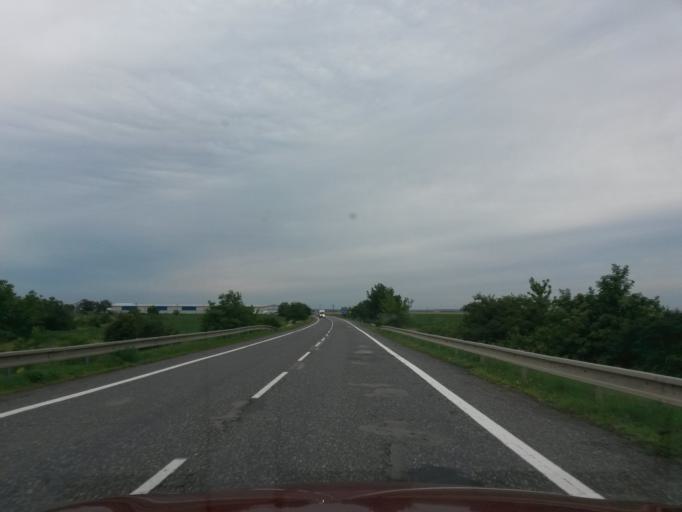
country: SK
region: Nitriansky
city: Zeliezovce
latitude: 48.1161
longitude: 18.6290
